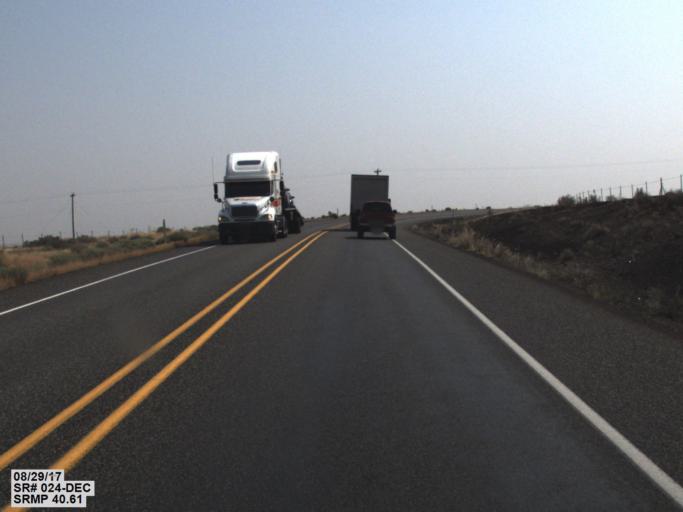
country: US
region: Washington
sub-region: Grant County
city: Desert Aire
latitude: 46.6041
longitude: -119.7300
